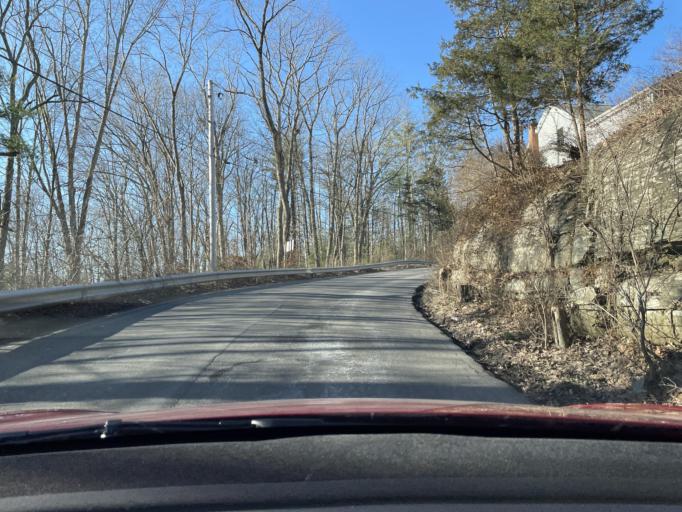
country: US
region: New York
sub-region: Ulster County
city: Zena
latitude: 42.0460
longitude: -74.0165
